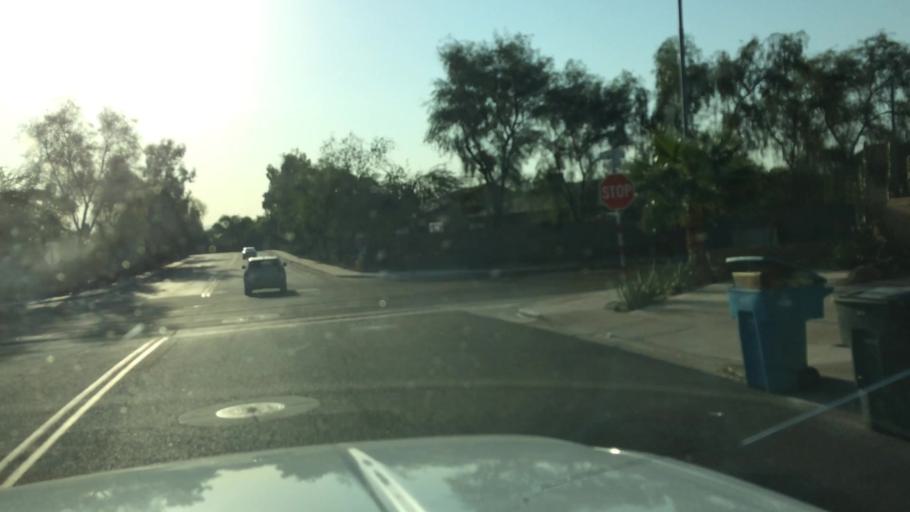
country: US
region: Arizona
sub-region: Maricopa County
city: Paradise Valley
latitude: 33.6186
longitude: -111.9434
